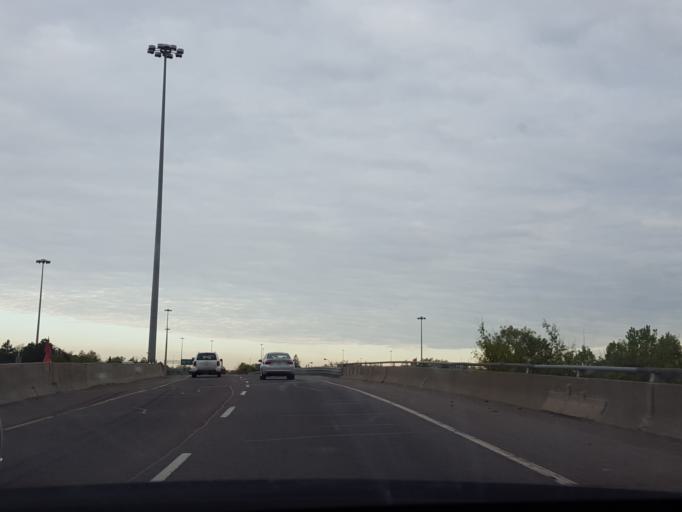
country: CA
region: Ontario
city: Etobicoke
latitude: 43.7111
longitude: -79.5036
